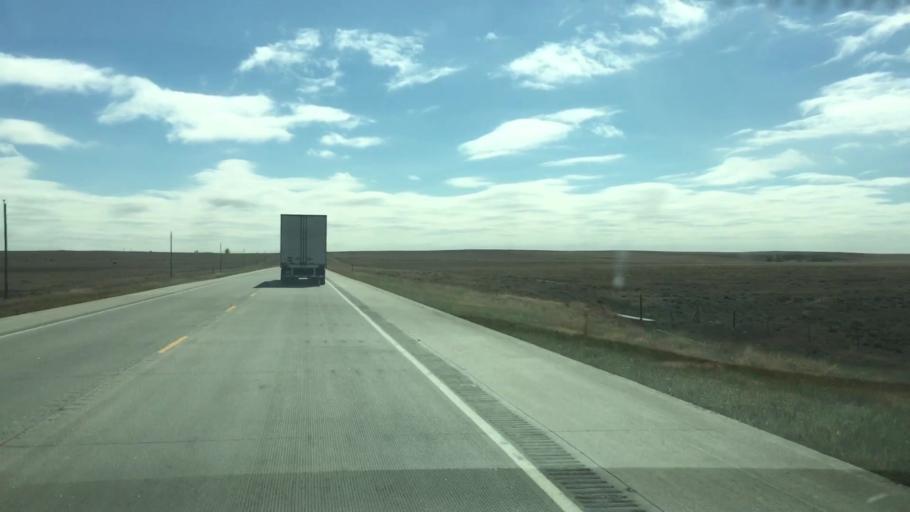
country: US
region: Colorado
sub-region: Lincoln County
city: Hugo
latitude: 39.0444
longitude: -103.3417
